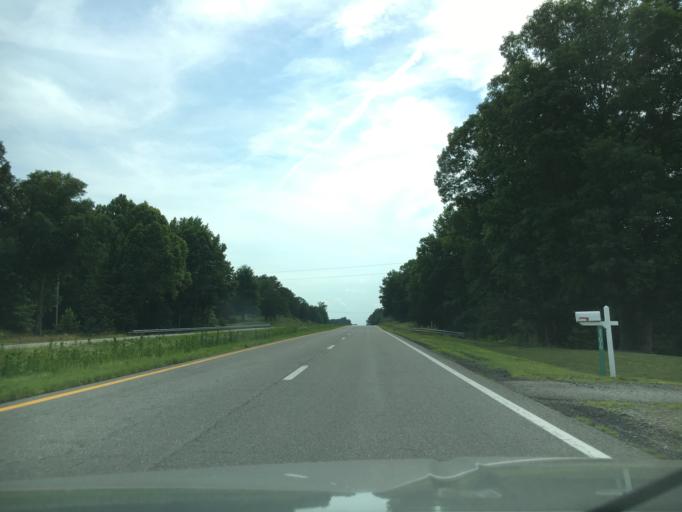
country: US
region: Virginia
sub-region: Mecklenburg County
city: Chase City
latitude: 36.8390
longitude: -78.6358
